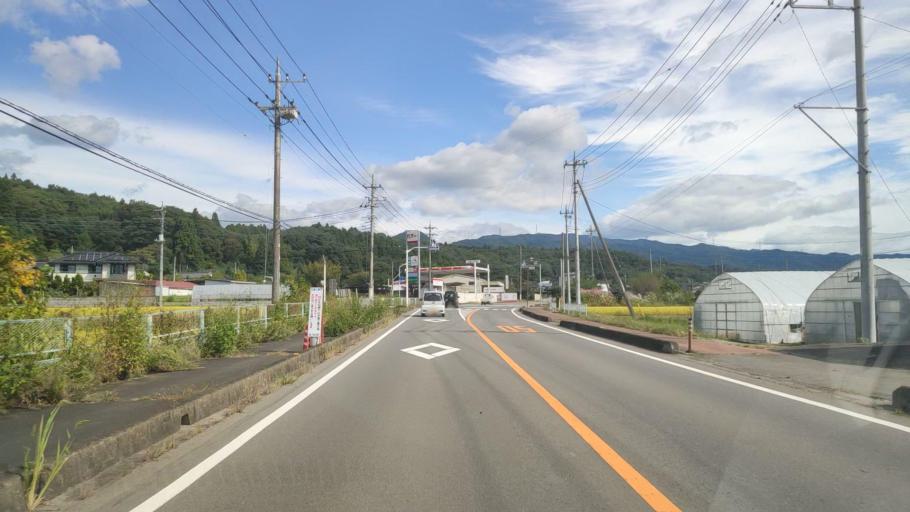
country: JP
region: Gunma
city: Nakanojomachi
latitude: 36.5988
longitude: 138.8638
